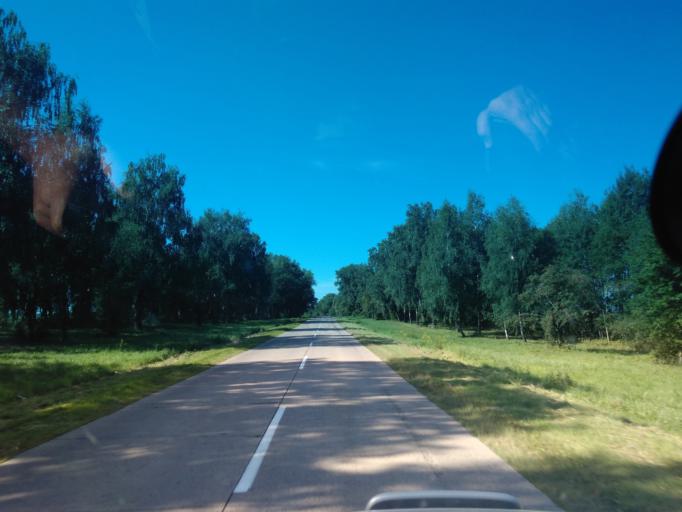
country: BY
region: Minsk
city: Stan'kava
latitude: 53.6455
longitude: 27.2979
